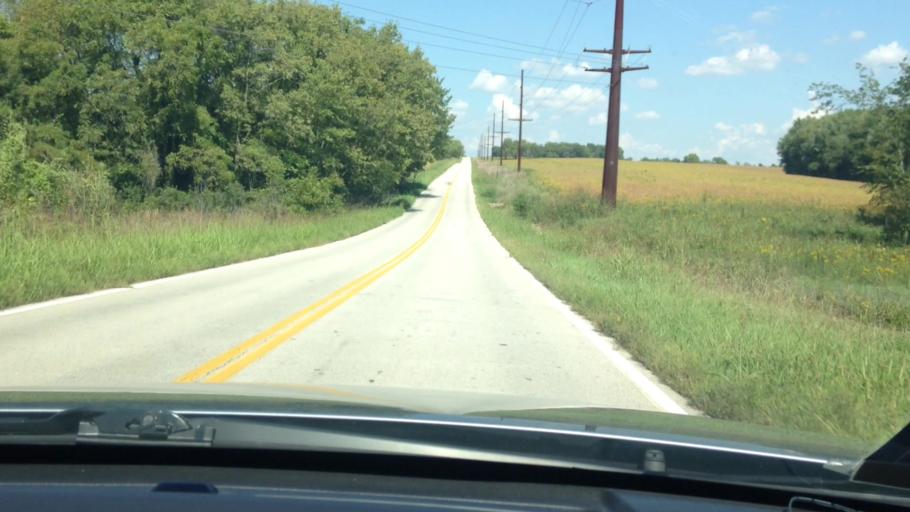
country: US
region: Missouri
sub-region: Platte County
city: Platte City
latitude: 39.3411
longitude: -94.7330
